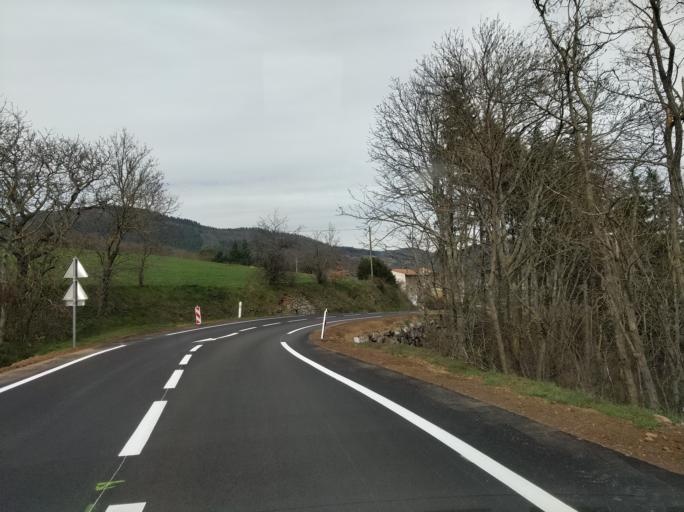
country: FR
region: Rhone-Alpes
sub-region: Departement de l'Ardeche
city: Satillieu
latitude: 45.1795
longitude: 4.6442
